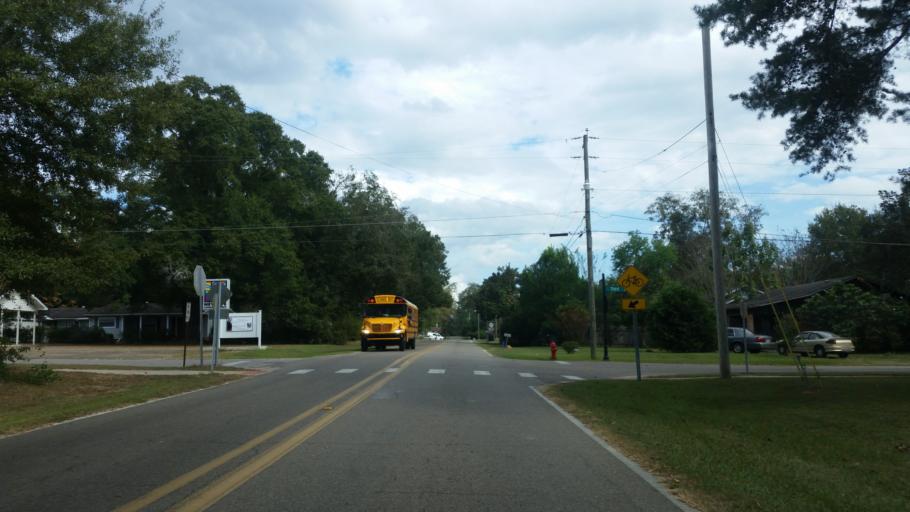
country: US
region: Mississippi
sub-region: Stone County
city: Wiggins
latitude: 30.8616
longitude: -89.1345
